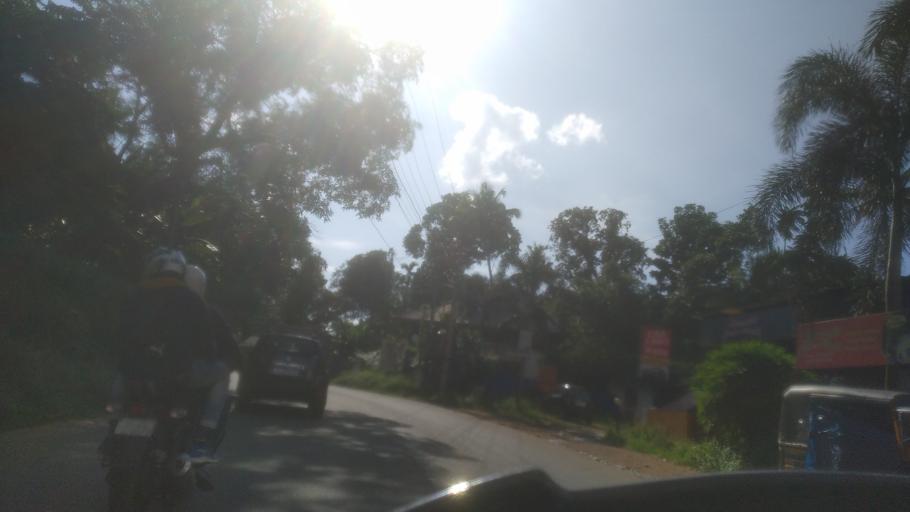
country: IN
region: Kerala
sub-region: Ernakulam
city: Muvattupula
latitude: 9.9882
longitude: 76.5685
